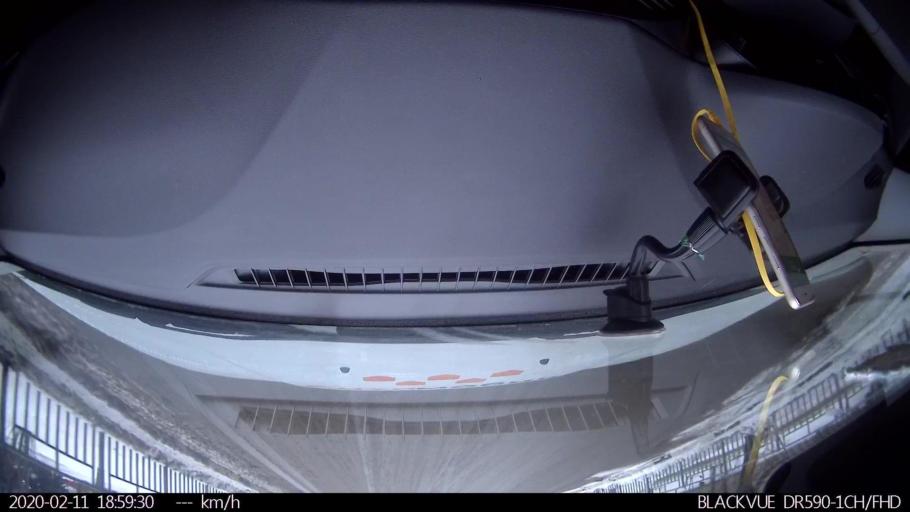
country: RU
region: Belgorod
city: Prokhorovka
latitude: 50.8330
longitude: 36.8578
